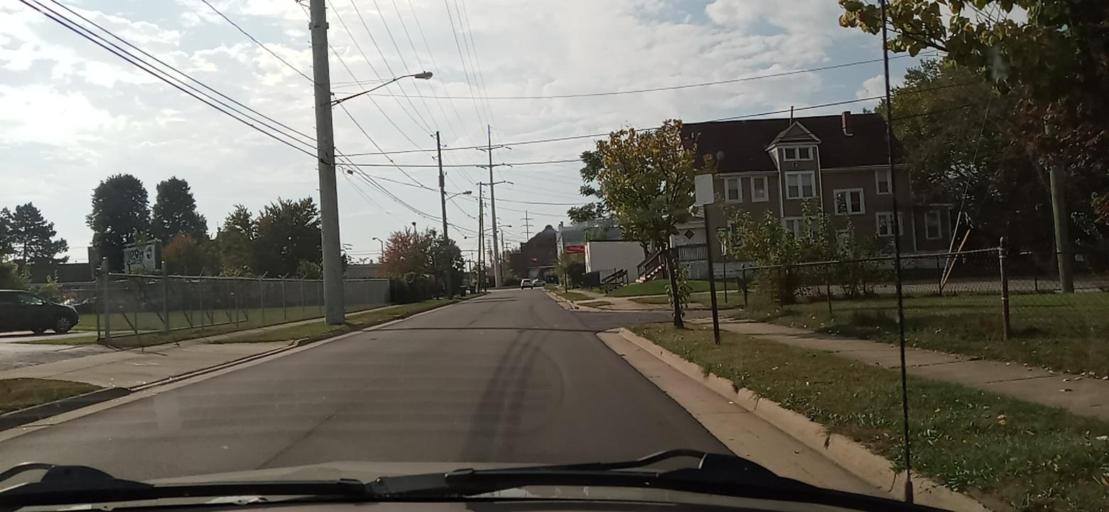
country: US
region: Ohio
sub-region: Summit County
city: Akron
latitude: 41.0514
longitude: -81.5415
